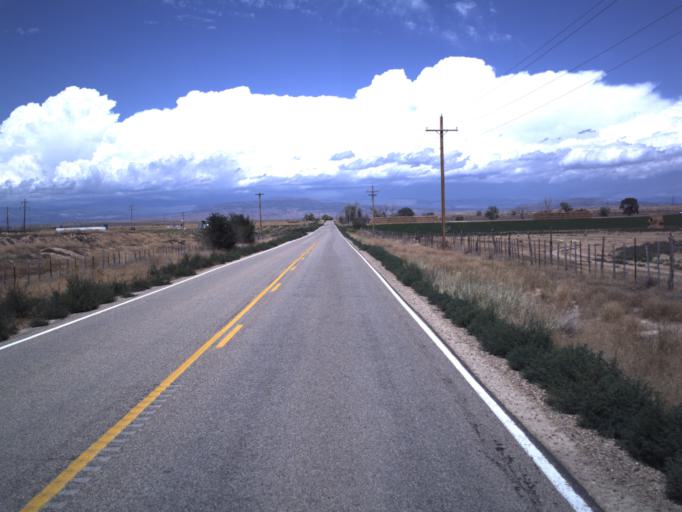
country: US
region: Utah
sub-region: Uintah County
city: Maeser
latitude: 40.2263
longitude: -109.6843
